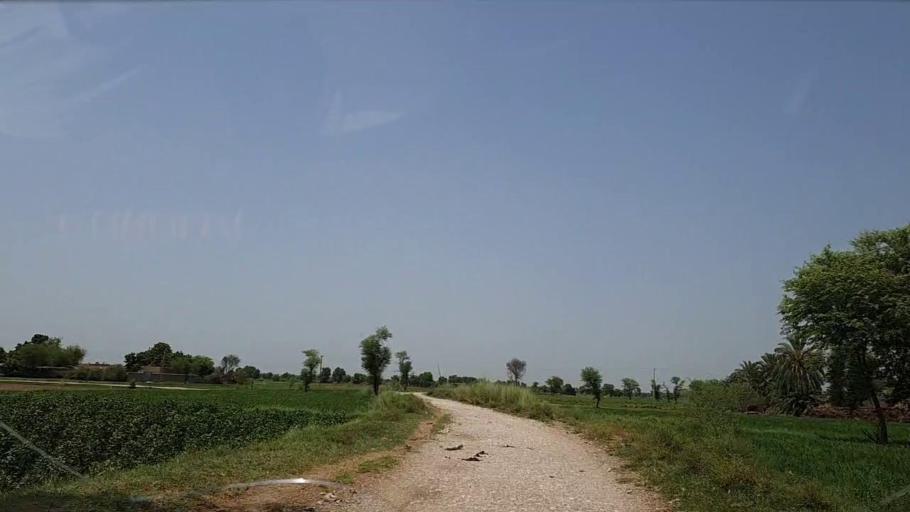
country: PK
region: Sindh
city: Tharu Shah
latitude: 26.9479
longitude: 68.0442
